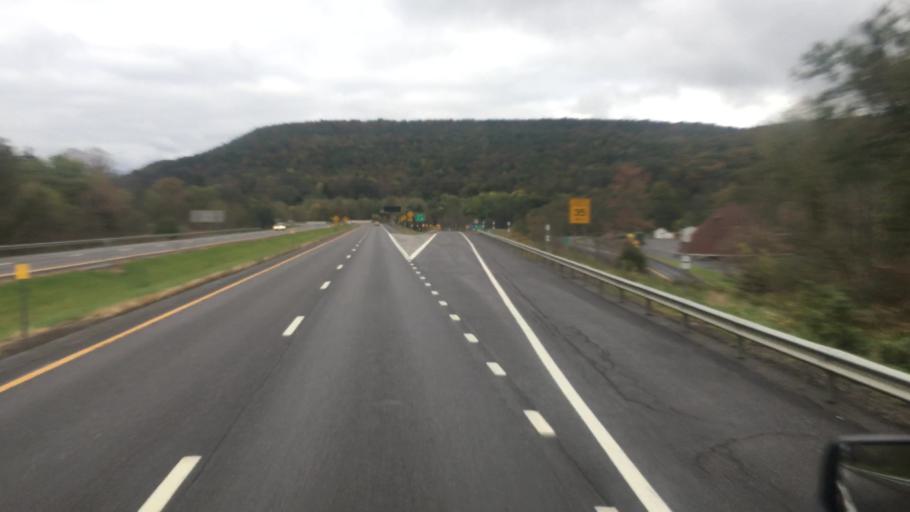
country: US
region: New York
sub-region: Broome County
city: Chenango Bridge
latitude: 42.1660
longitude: -75.8277
